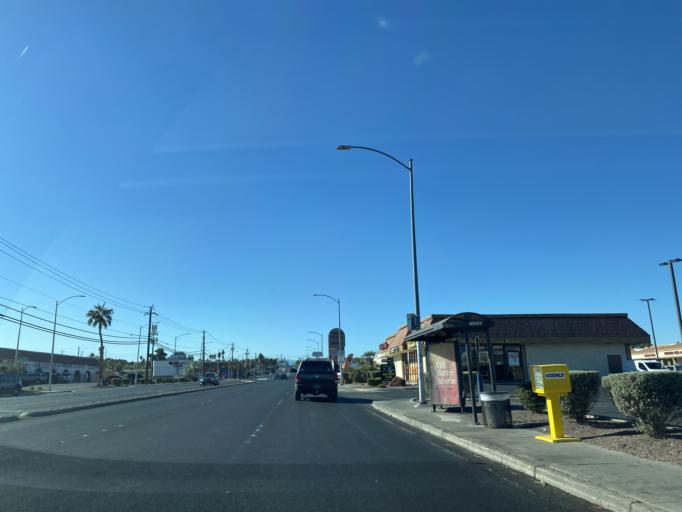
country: US
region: Nevada
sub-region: Clark County
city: Whitney
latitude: 36.1004
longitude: -115.0735
